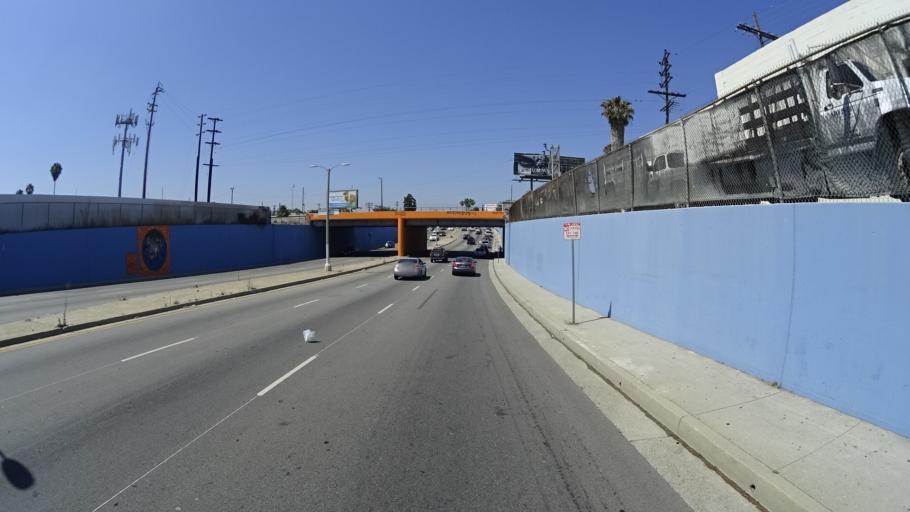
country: US
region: California
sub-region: Los Angeles County
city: Van Nuys
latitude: 34.2075
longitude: -118.4310
